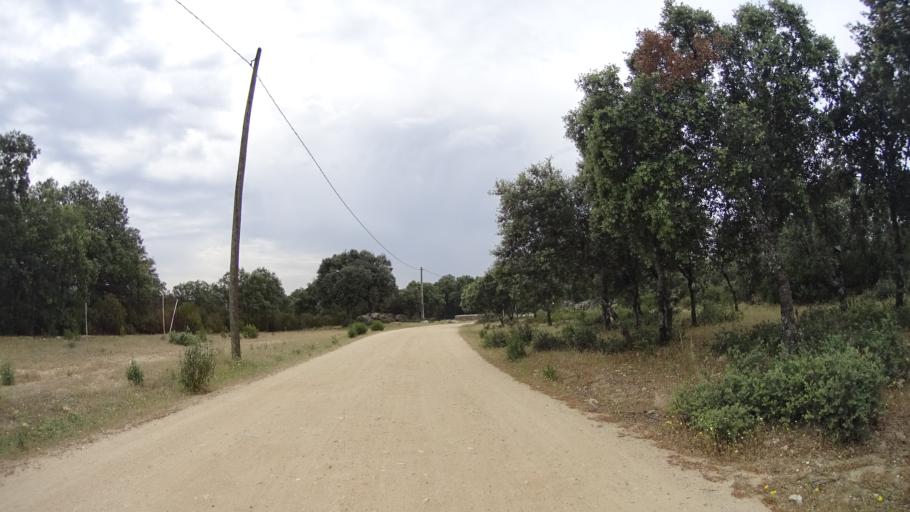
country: ES
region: Madrid
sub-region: Provincia de Madrid
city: Colmenarejo
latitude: 40.5616
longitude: -4.0345
